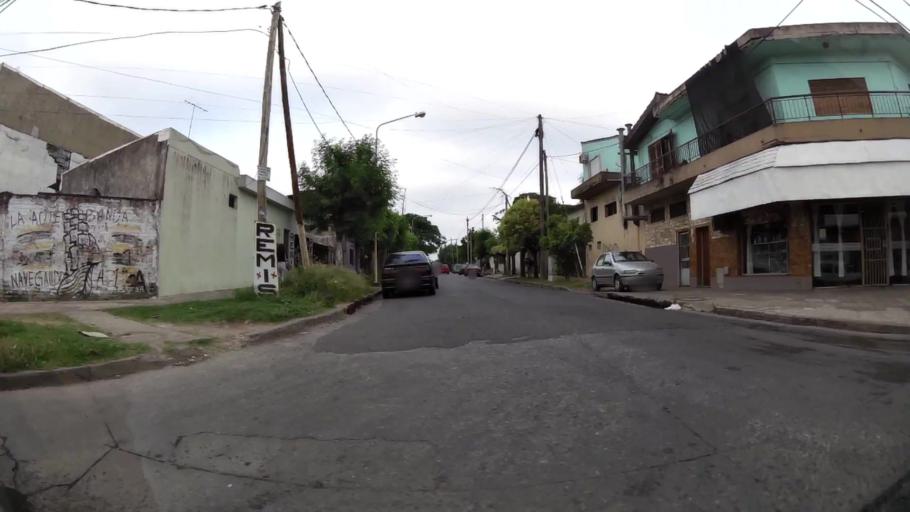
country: AR
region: Buenos Aires
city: San Justo
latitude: -34.7042
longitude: -58.5758
